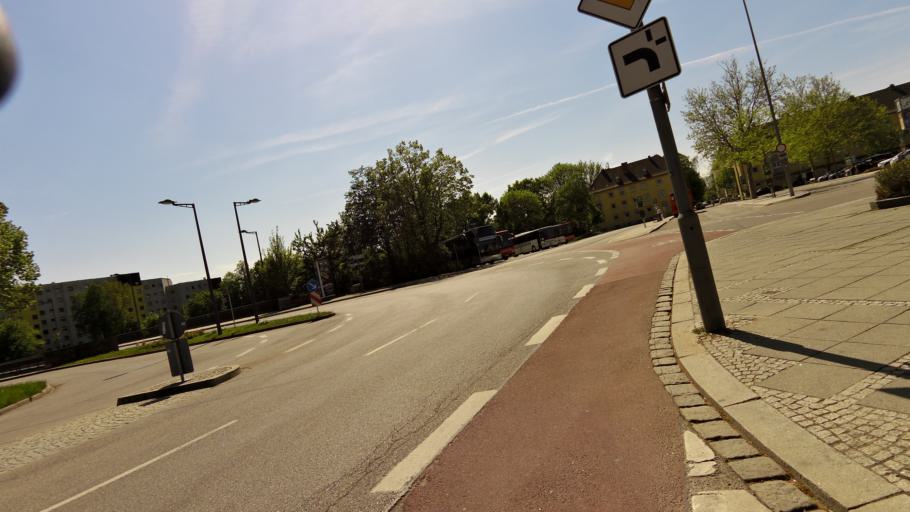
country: DE
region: Bavaria
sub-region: Lower Bavaria
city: Landshut
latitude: 48.5468
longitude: 12.1366
